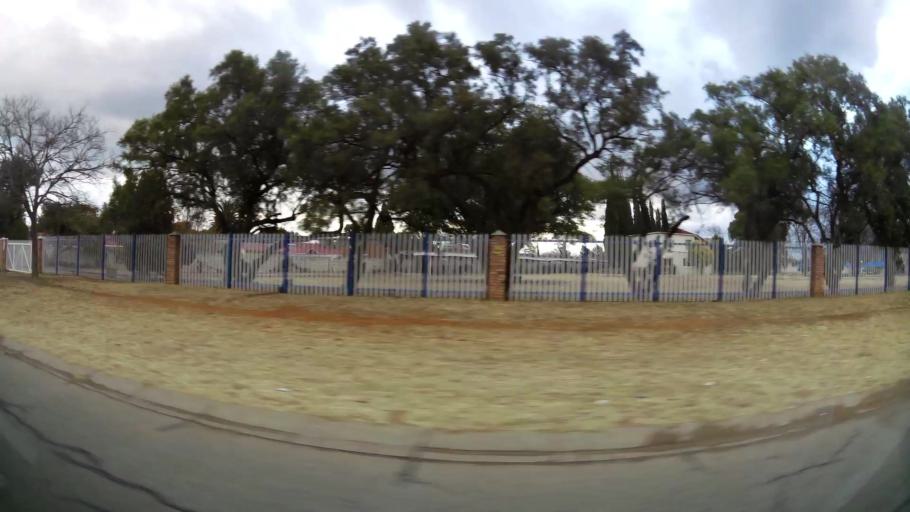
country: ZA
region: Orange Free State
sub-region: Lejweleputswa District Municipality
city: Welkom
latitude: -27.9553
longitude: 26.7266
